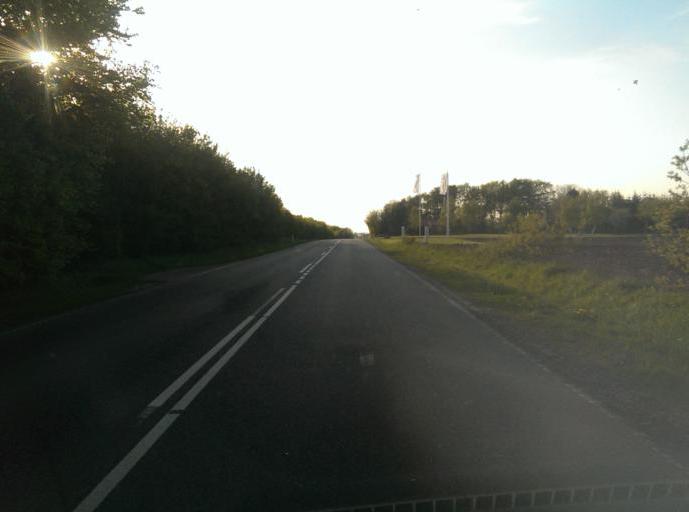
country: DK
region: South Denmark
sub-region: Esbjerg Kommune
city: Tjaereborg
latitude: 55.4994
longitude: 8.5679
